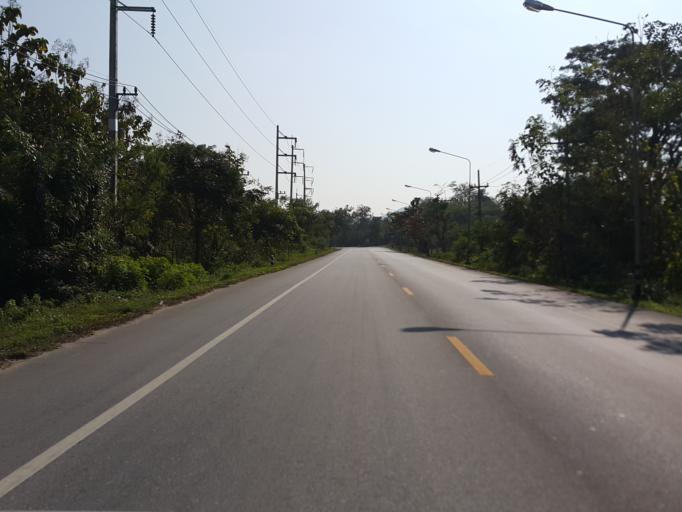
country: TH
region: Lampang
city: Chae Hom
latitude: 18.6543
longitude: 99.5380
